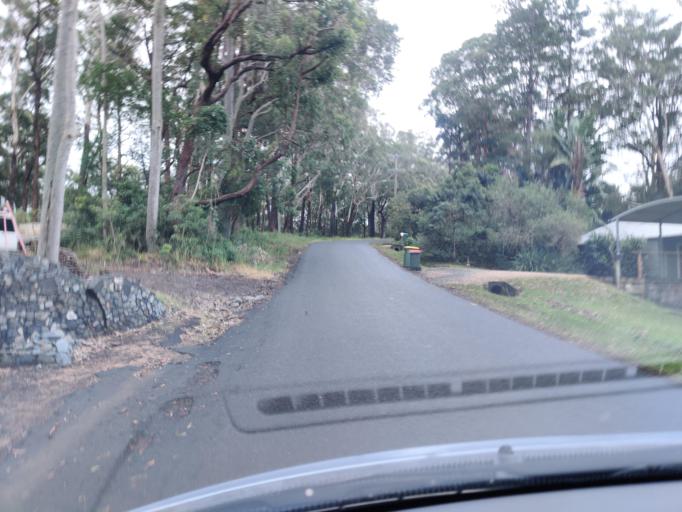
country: AU
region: New South Wales
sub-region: Great Lakes
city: Forster
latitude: -32.3855
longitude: 152.5042
